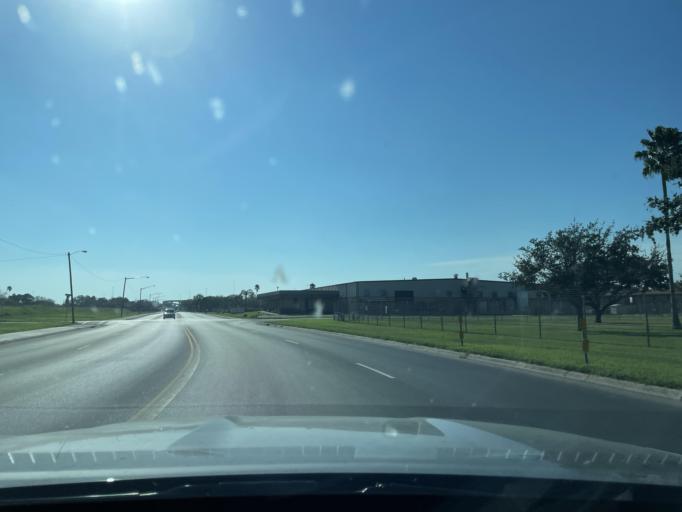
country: US
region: Texas
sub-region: Cameron County
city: Harlingen
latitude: 26.1996
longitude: -97.7105
